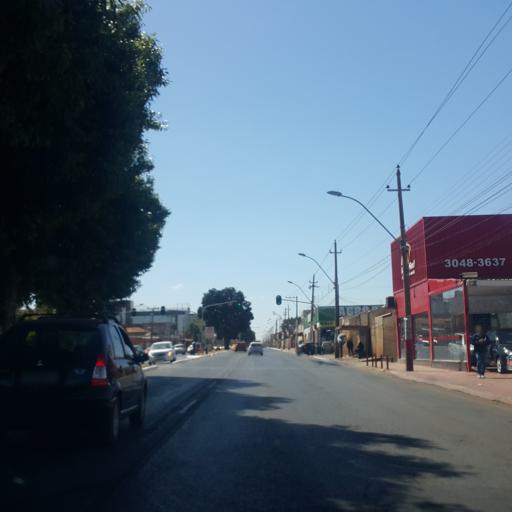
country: BR
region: Federal District
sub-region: Brasilia
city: Brasilia
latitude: -15.8027
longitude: -48.0660
